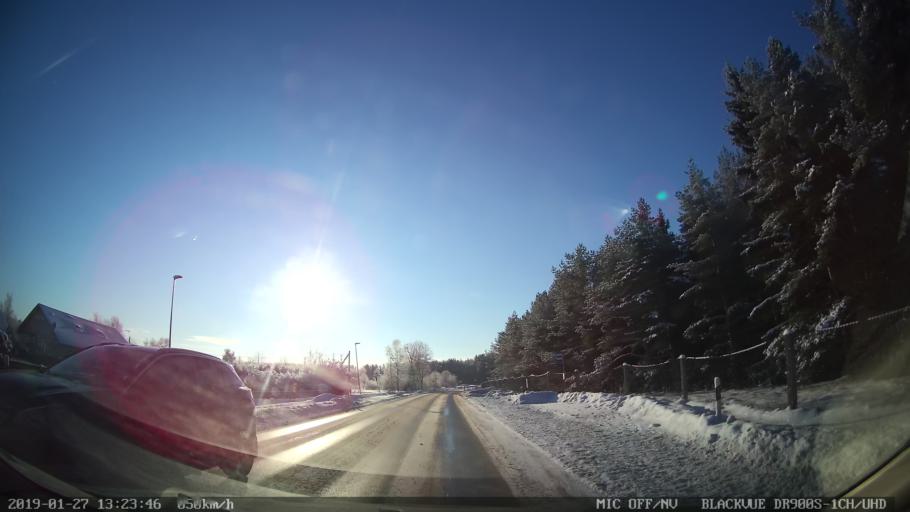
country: EE
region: Harju
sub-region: Tallinna linn
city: Tallinn
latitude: 59.4042
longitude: 24.7922
